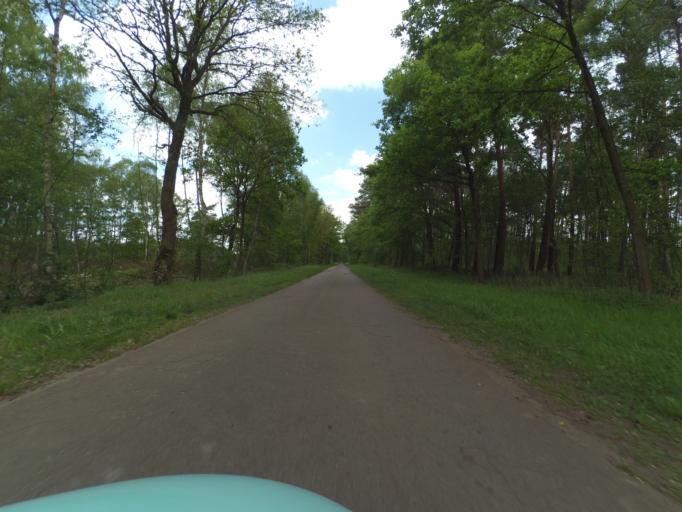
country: DE
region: Lower Saxony
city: Wietze
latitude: 52.5790
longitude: 9.8285
